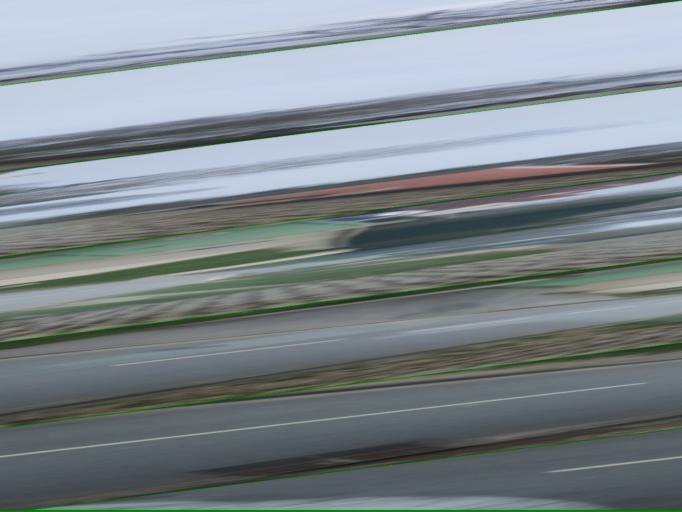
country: FR
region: Ile-de-France
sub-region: Departement des Yvelines
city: Houdan
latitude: 48.8370
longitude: 1.6083
